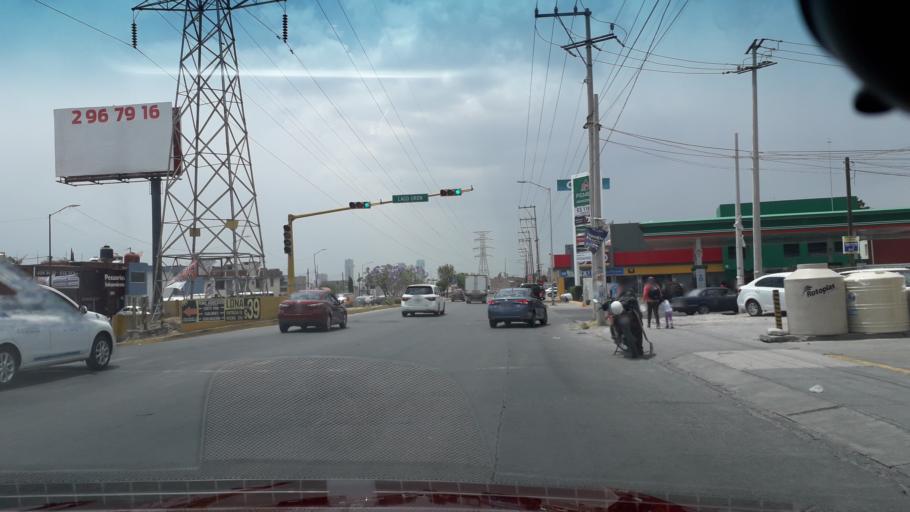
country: MX
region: Puebla
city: Tlazcalancingo
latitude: 19.0056
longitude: -98.2405
